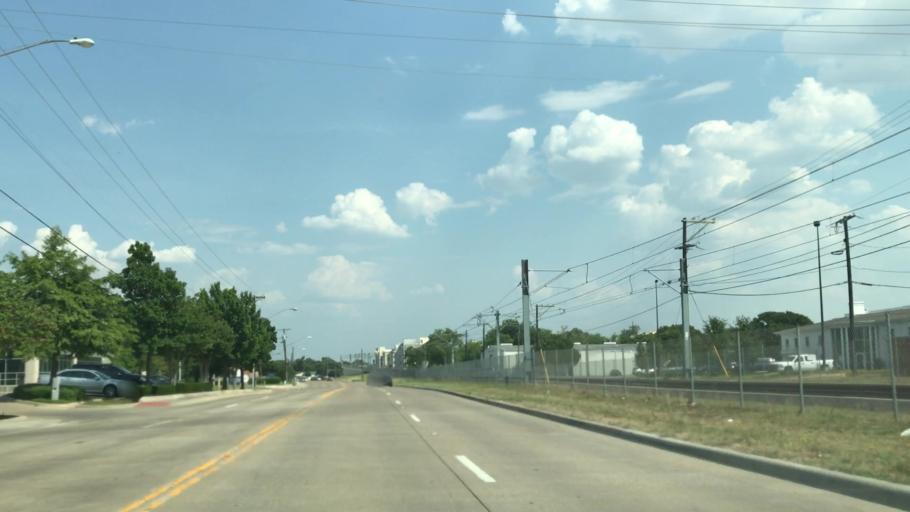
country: US
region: Texas
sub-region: Dallas County
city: University Park
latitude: 32.8274
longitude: -96.8384
